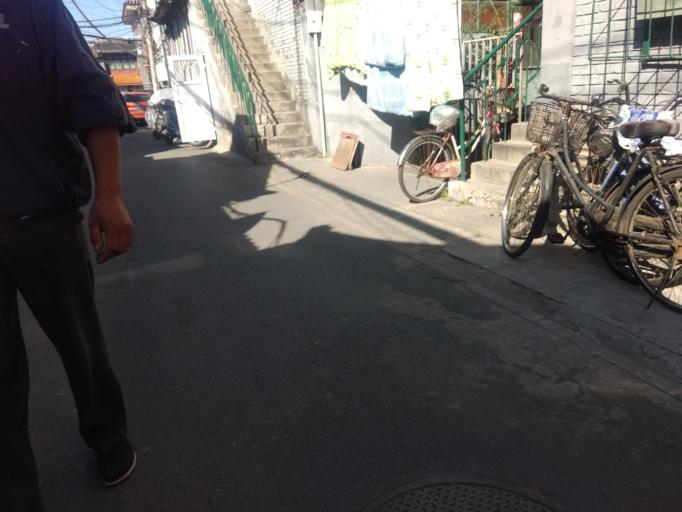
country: CN
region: Beijing
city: Beijing
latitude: 39.8932
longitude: 116.3817
